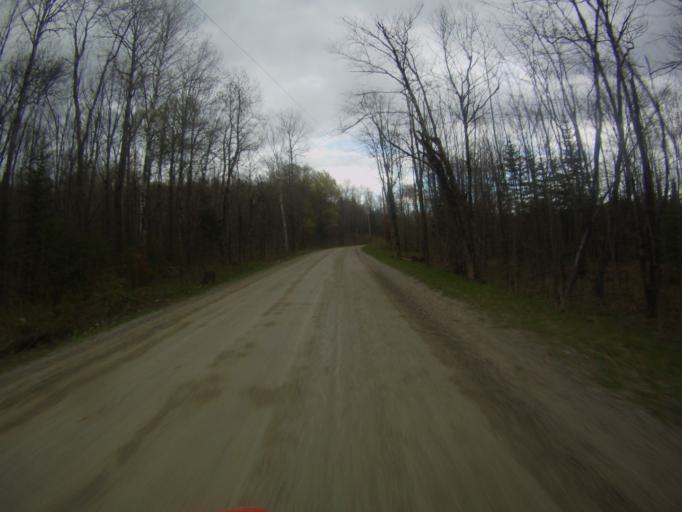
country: US
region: Vermont
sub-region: Addison County
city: Bristol
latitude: 44.0517
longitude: -73.0126
